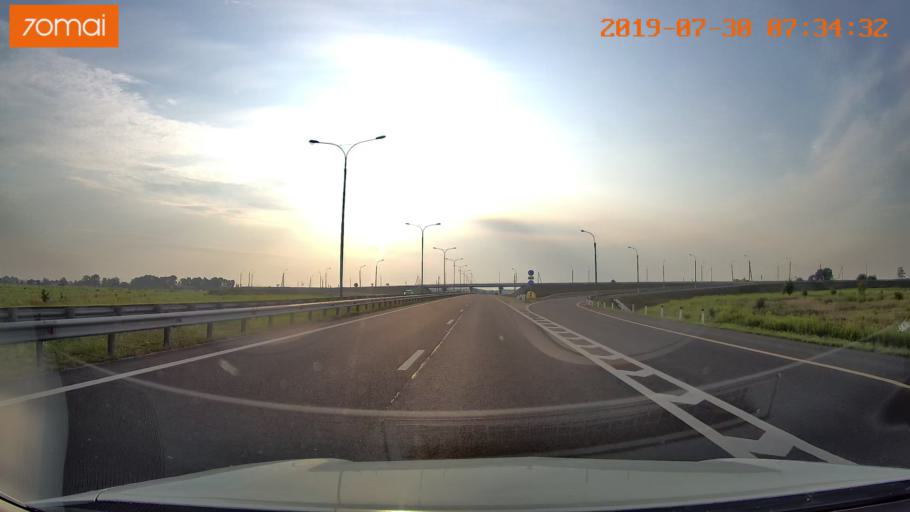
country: RU
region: Kaliningrad
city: Gvardeysk
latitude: 54.6722
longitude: 21.0748
